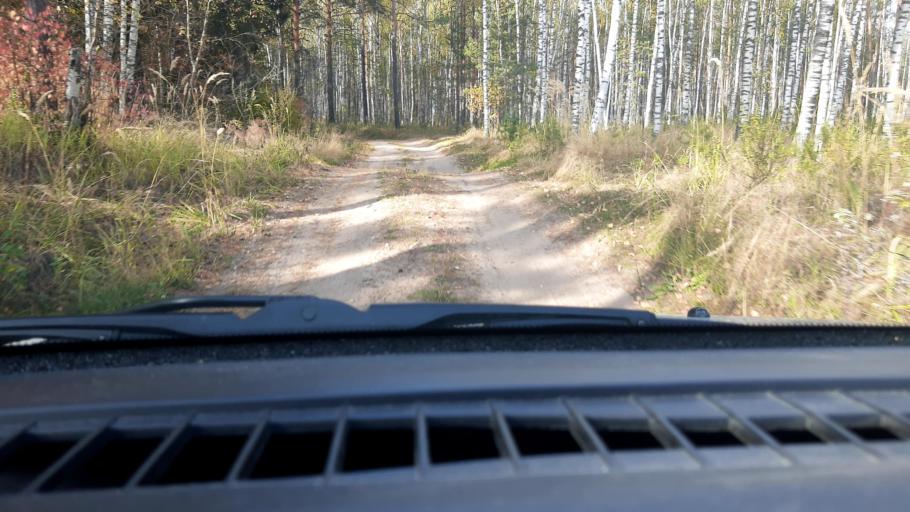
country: RU
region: Nizjnij Novgorod
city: Lukino
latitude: 56.3892
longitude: 43.6290
